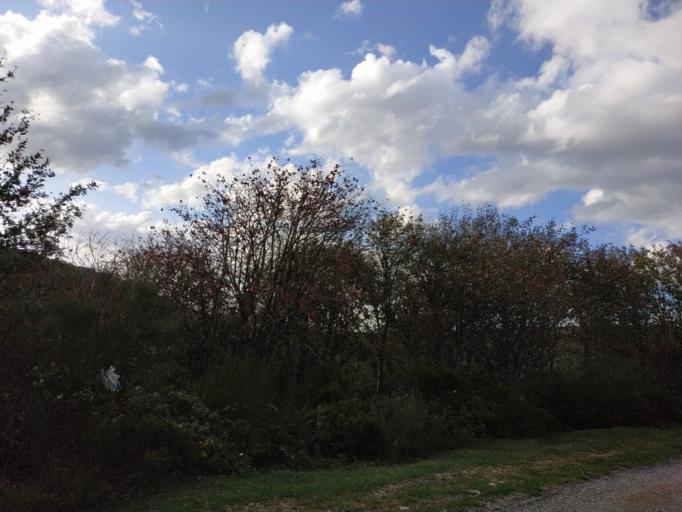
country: ES
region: Castille and Leon
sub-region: Provincia de Leon
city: Candin
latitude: 42.8771
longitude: -6.8310
